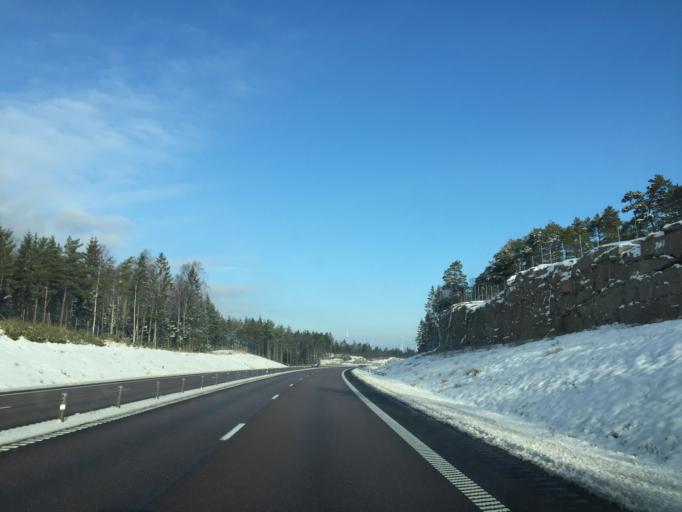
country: SE
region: Vaestra Goetaland
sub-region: Tanums Kommun
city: Tanumshede
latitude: 58.7933
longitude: 11.2782
